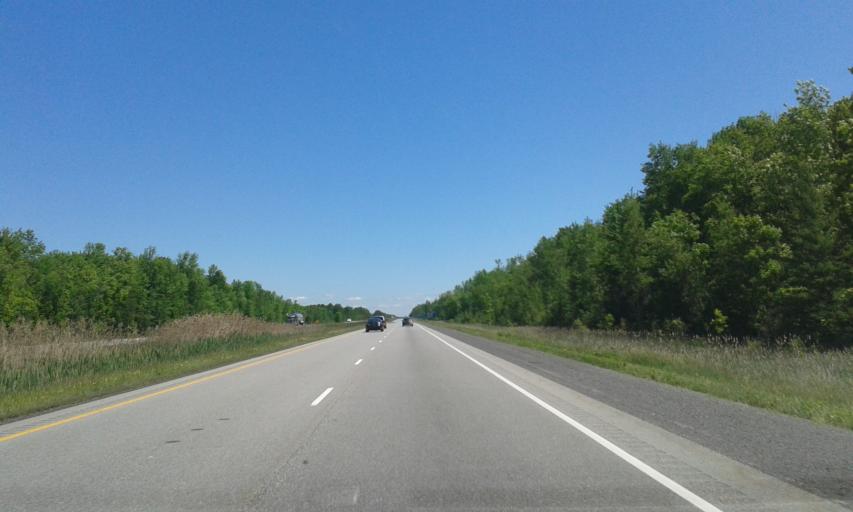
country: US
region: New York
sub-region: St. Lawrence County
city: Ogdensburg
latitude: 44.7917
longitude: -75.4352
